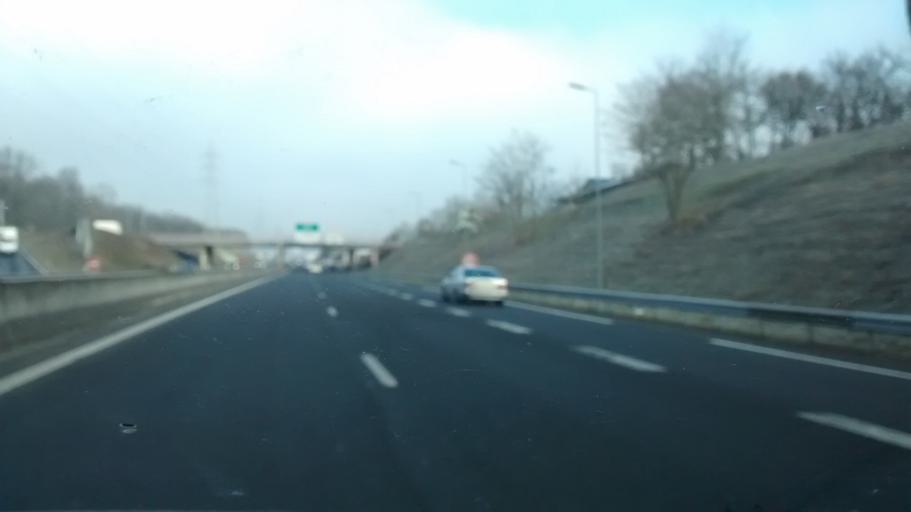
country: FR
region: Centre
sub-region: Departement d'Indre-et-Loire
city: Joue-les-Tours
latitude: 47.3445
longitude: 0.6463
